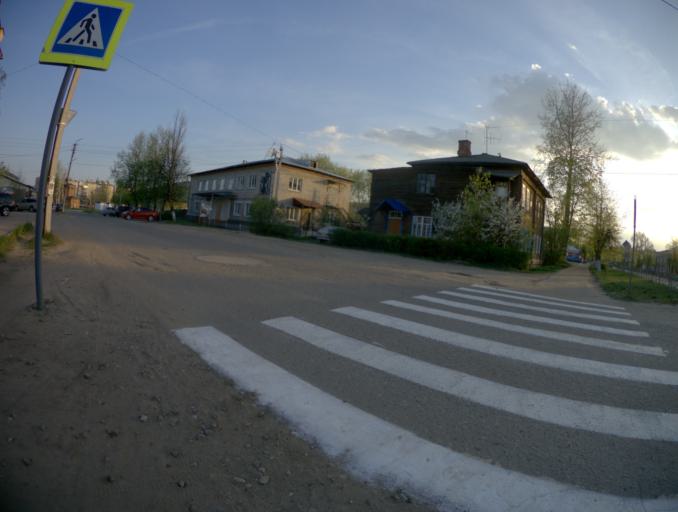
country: RU
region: Ivanovo
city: Yuzha
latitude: 56.5836
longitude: 42.0142
